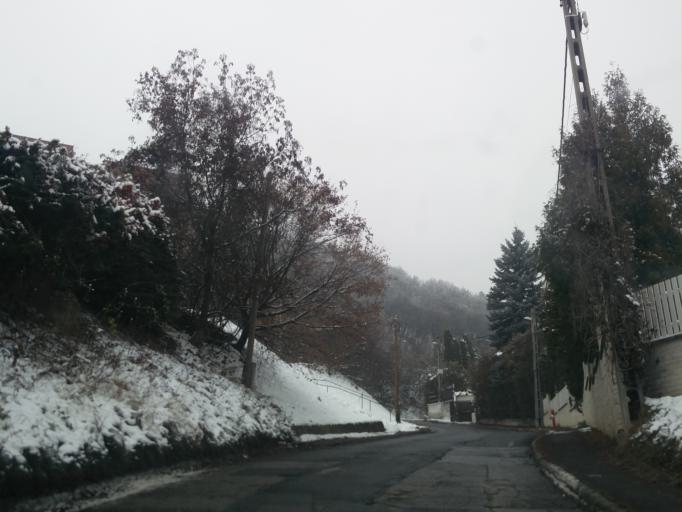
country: HU
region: Budapest
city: Budapest III. keruelet
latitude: 47.5366
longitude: 19.0243
